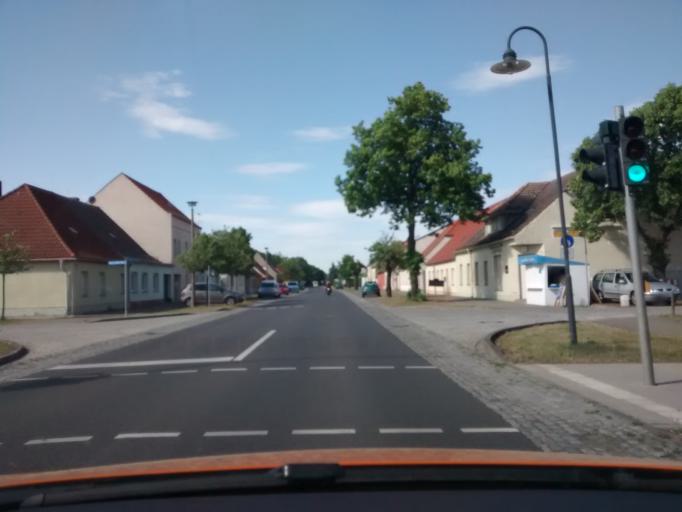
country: DE
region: Brandenburg
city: Juterbog
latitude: 52.0226
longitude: 13.1042
